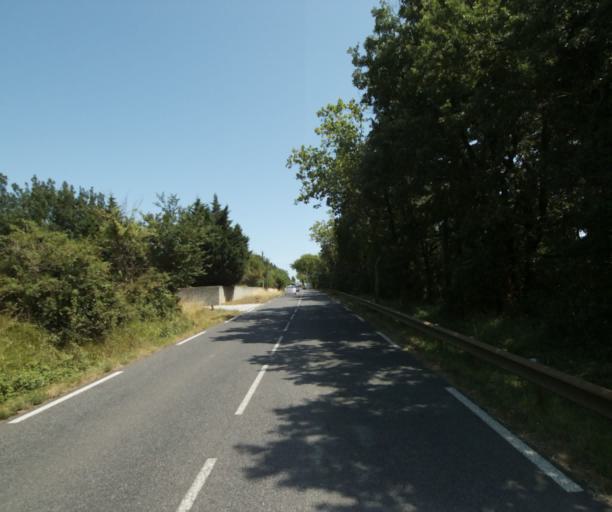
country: FR
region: Midi-Pyrenees
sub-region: Departement de la Haute-Garonne
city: Saint-Felix-Lauragais
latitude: 43.4545
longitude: 1.8716
